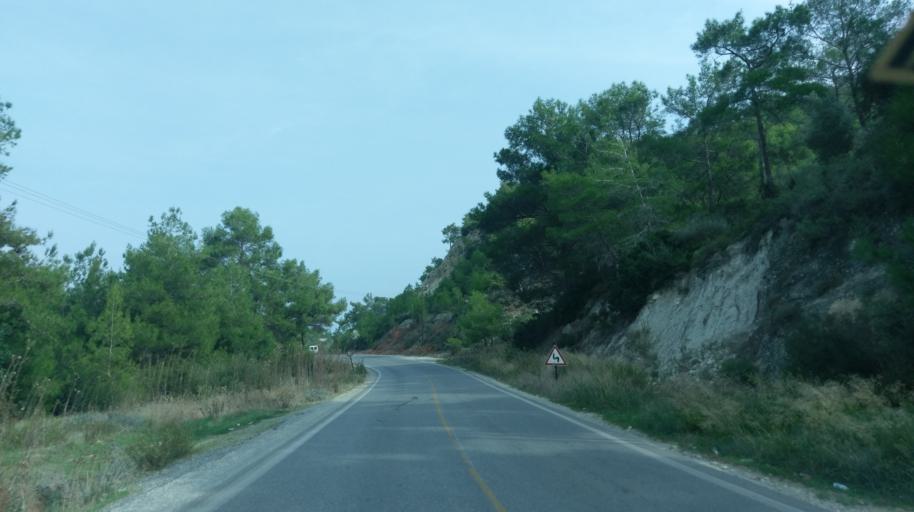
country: CY
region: Keryneia
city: Lapithos
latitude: 35.3409
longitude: 33.0741
